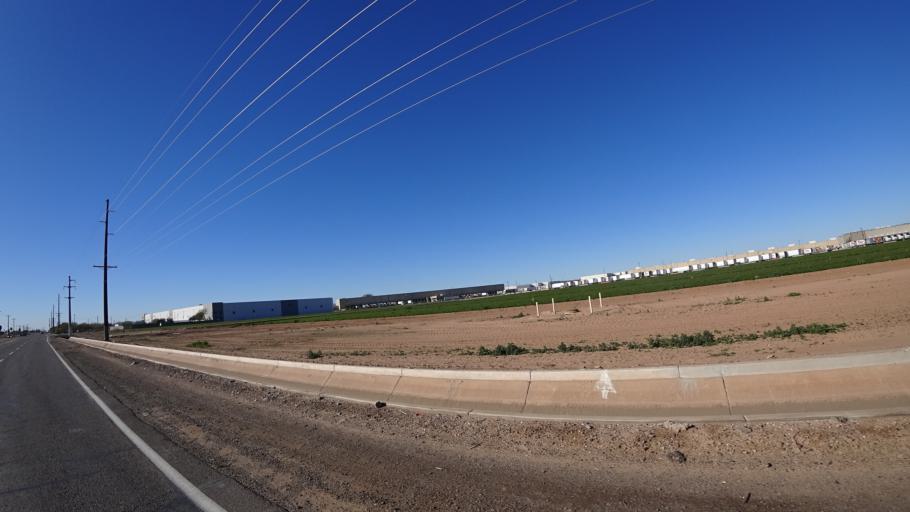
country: US
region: Arizona
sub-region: Maricopa County
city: Tolleson
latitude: 33.4357
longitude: -112.2783
